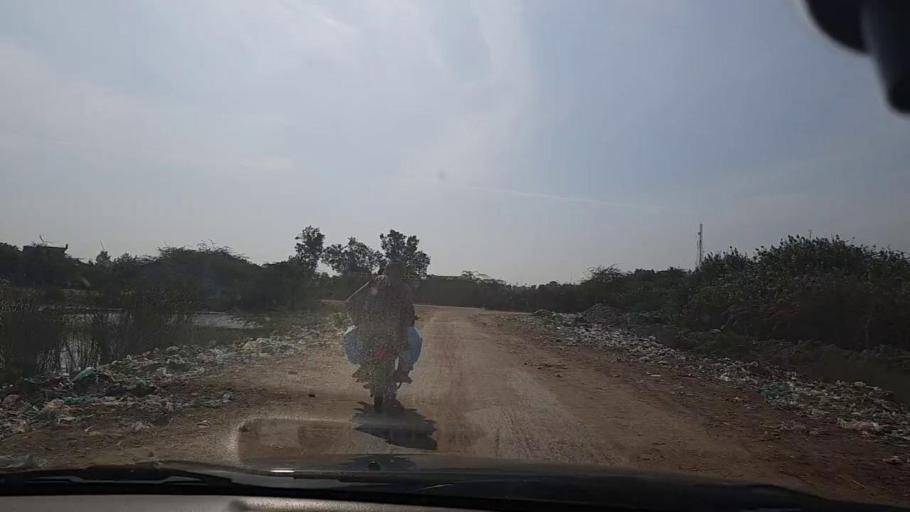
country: PK
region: Sindh
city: Mirpur Batoro
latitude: 24.7325
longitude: 68.2647
